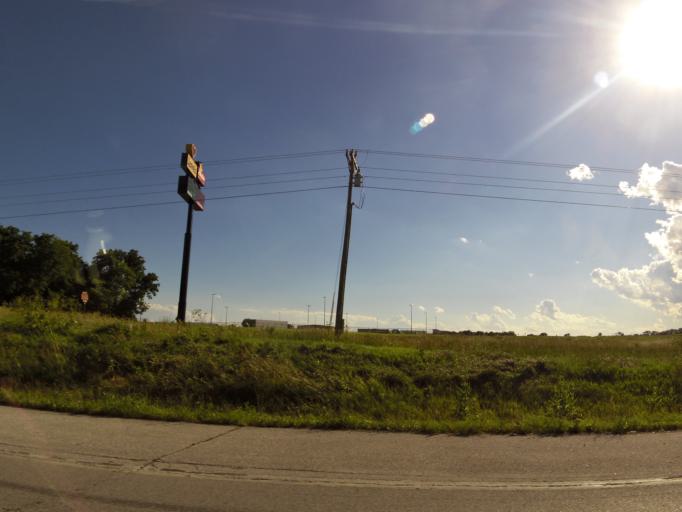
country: US
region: Missouri
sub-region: Ralls County
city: New London
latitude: 39.5767
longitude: -91.4027
